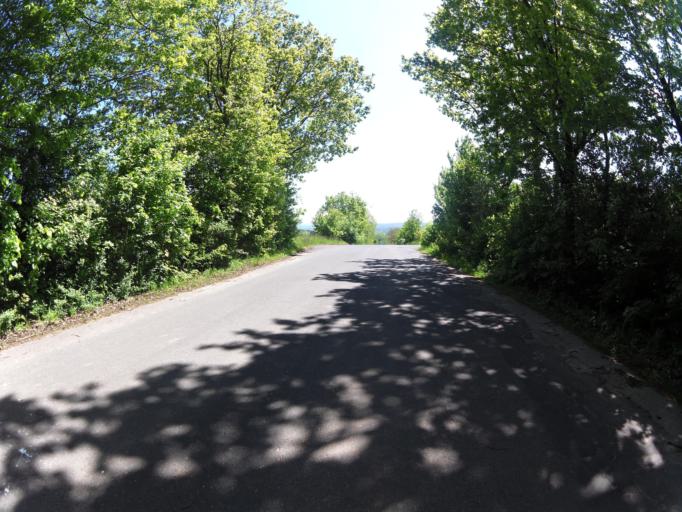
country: DE
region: Thuringia
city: Dankmarshausen
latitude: 50.9584
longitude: 10.0083
